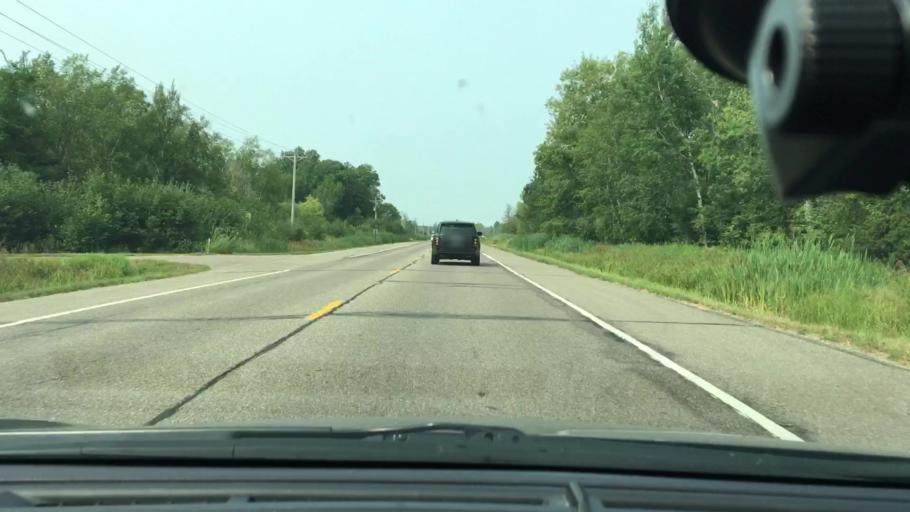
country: US
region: Minnesota
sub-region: Crow Wing County
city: Brainerd
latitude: 46.3985
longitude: -94.2123
